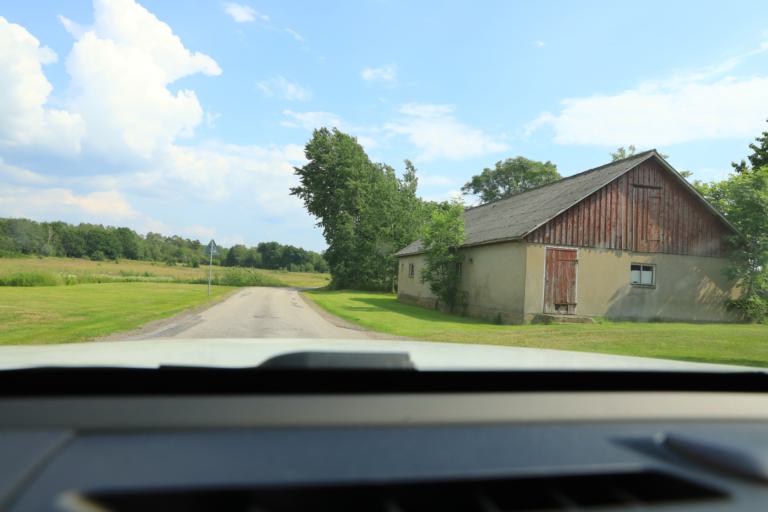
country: SE
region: Halland
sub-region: Varbergs Kommun
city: Varberg
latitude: 57.1579
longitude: 12.3151
